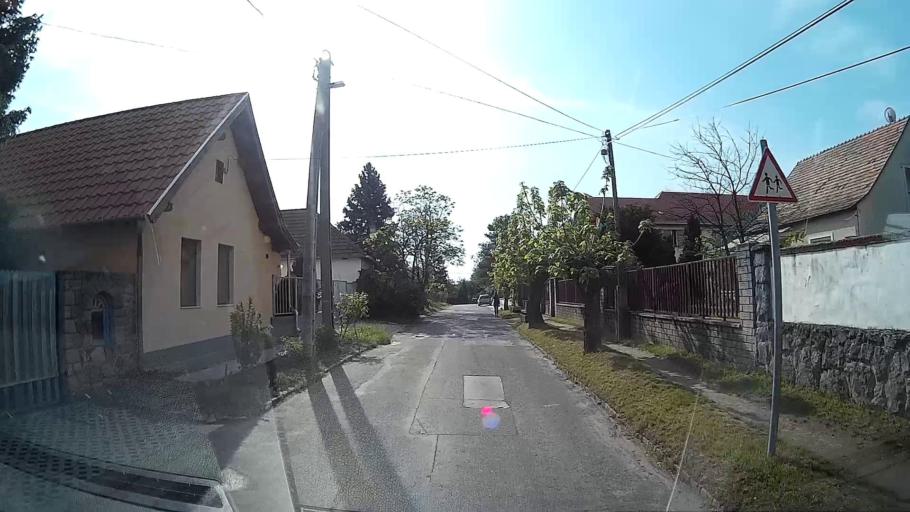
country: HU
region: Pest
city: God
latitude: 47.6882
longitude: 19.1051
